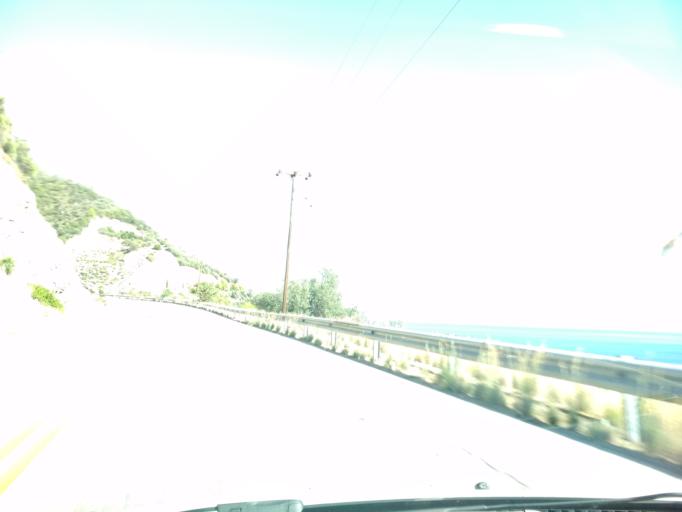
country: GR
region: Central Greece
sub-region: Nomos Evvoias
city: Oreoi
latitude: 38.8430
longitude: 23.0755
